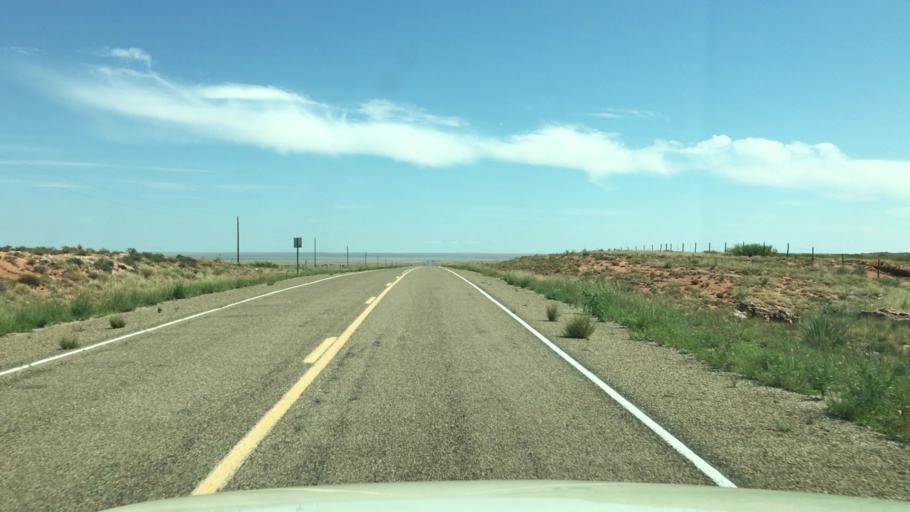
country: US
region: New Mexico
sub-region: Chaves County
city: Roswell
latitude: 33.9751
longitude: -104.5773
